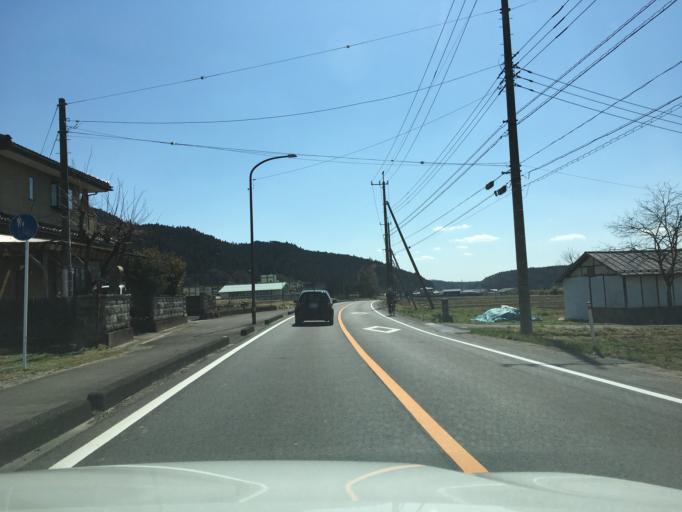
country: JP
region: Tochigi
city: Kuroiso
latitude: 36.9750
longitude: 140.1602
